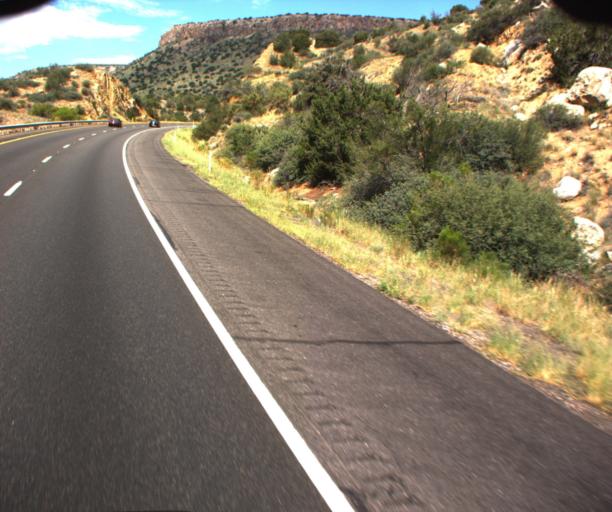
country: US
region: Arizona
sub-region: Yavapai County
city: Camp Verde
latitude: 34.5381
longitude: -111.9169
